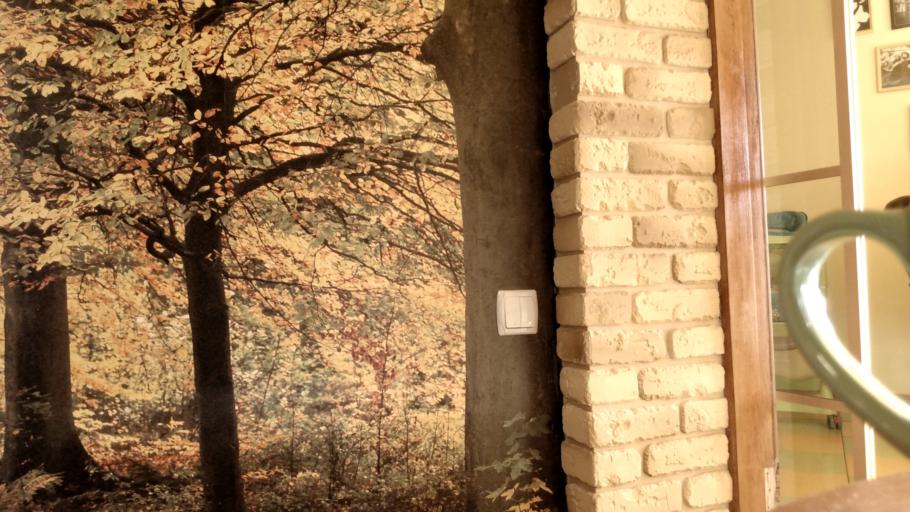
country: RU
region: Vologda
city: Imeni Zhelyabova
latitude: 58.8025
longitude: 36.8903
